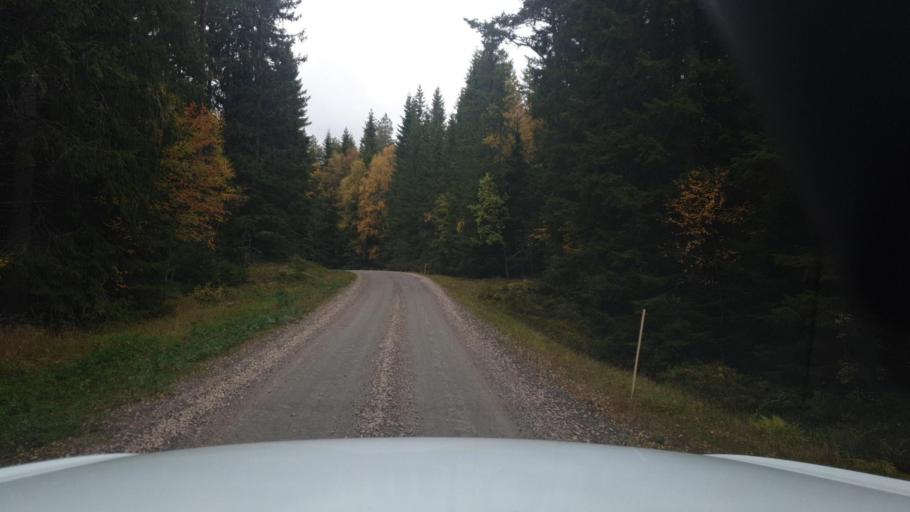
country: SE
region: Vaermland
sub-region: Eda Kommun
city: Charlottenberg
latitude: 60.1426
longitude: 12.5975
